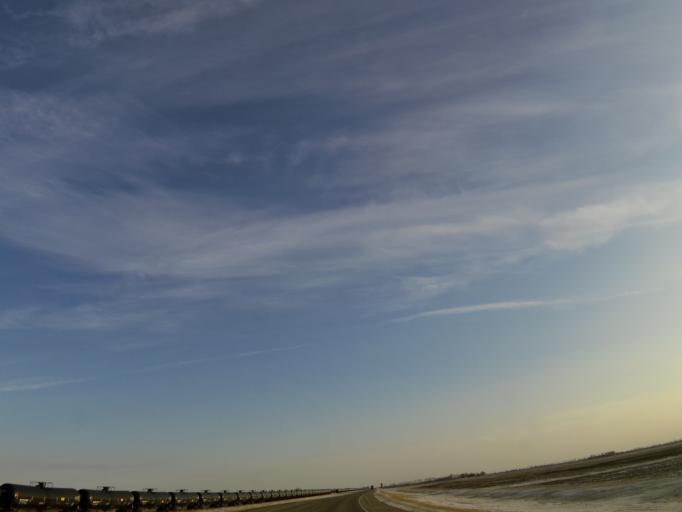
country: US
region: North Dakota
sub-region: Walsh County
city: Grafton
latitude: 48.5042
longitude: -97.4373
